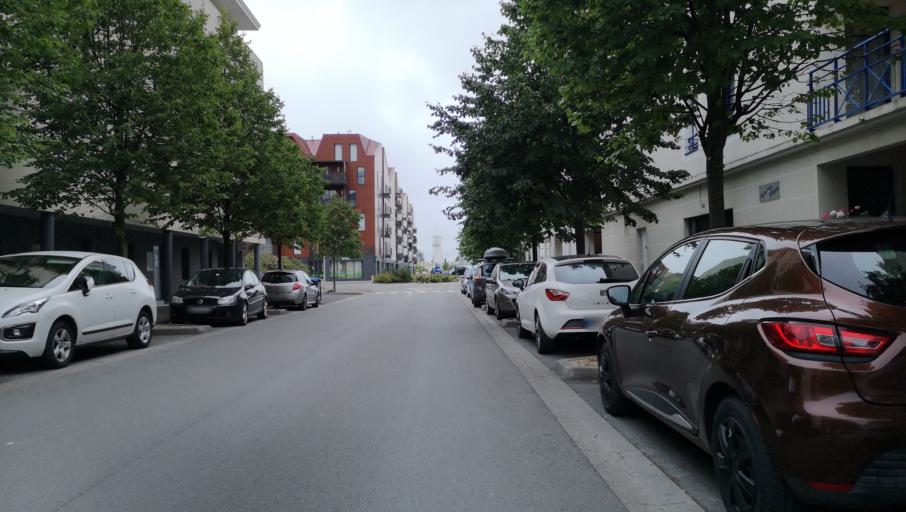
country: FR
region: Pays de la Loire
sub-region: Departement de la Vendee
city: Les Sables-d'Olonne
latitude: 46.5012
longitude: -1.7842
